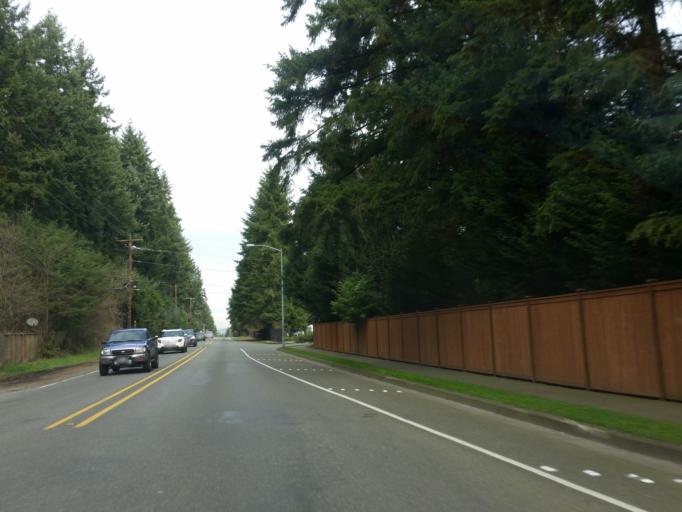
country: US
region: Washington
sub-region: Pierce County
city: South Hill
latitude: 47.1594
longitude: -122.2563
